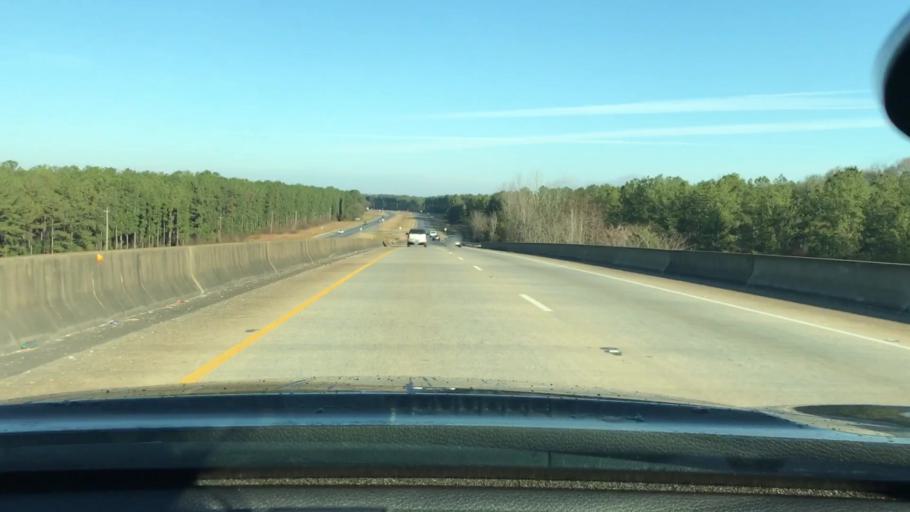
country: US
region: Alabama
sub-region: Talladega County
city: Childersburg
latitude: 33.2920
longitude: -86.3655
